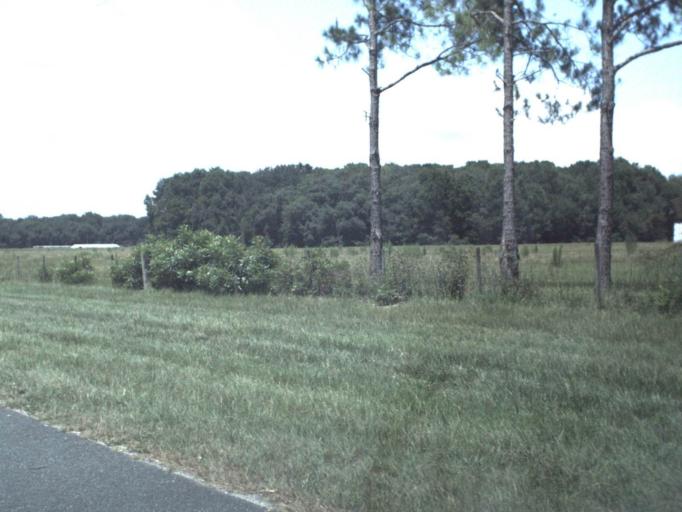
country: US
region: Florida
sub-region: Lafayette County
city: Mayo
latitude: 29.8912
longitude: -82.9549
